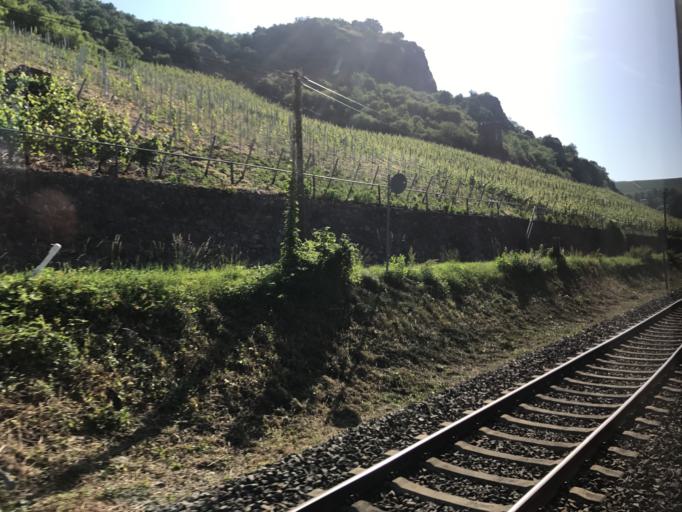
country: DE
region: Rheinland-Pfalz
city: Schlossbockelheim
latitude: 49.7986
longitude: 7.7512
